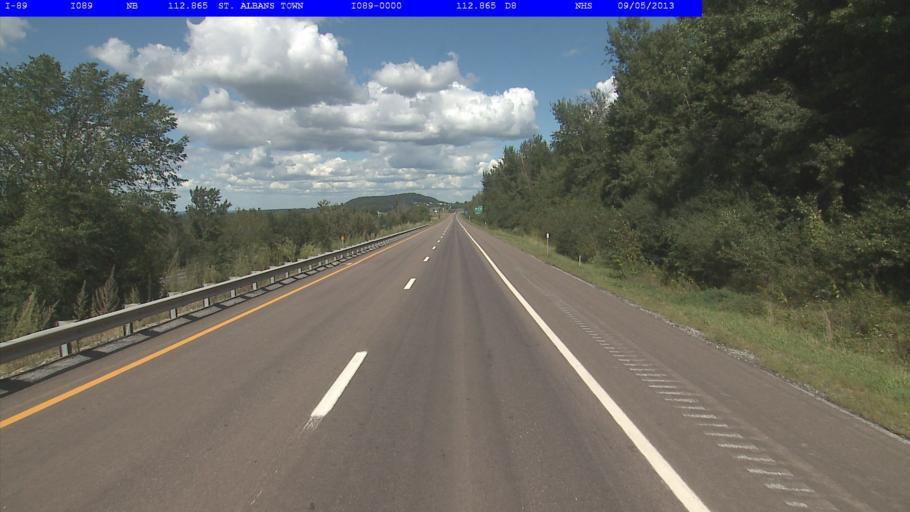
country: US
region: Vermont
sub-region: Franklin County
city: Saint Albans
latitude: 44.7823
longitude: -73.0728
